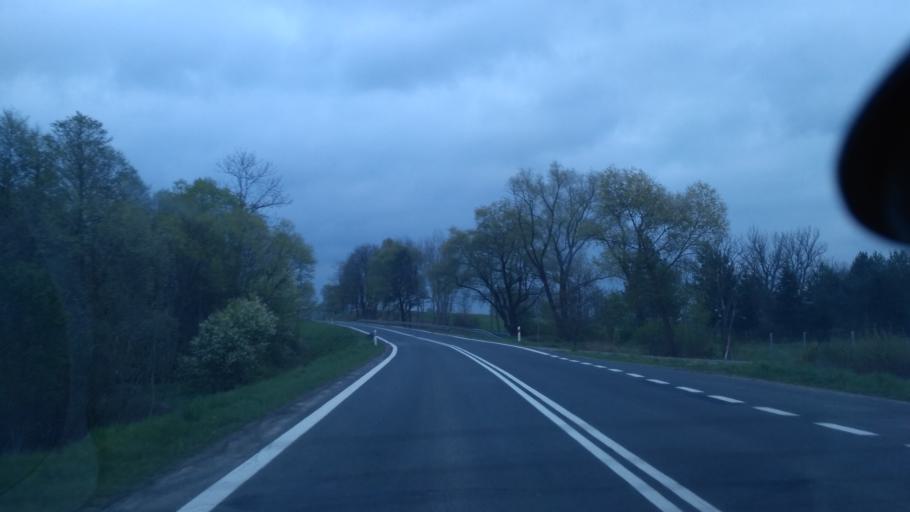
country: PL
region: Subcarpathian Voivodeship
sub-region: Powiat sanocki
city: Zagorz
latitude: 49.5324
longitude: 22.2888
